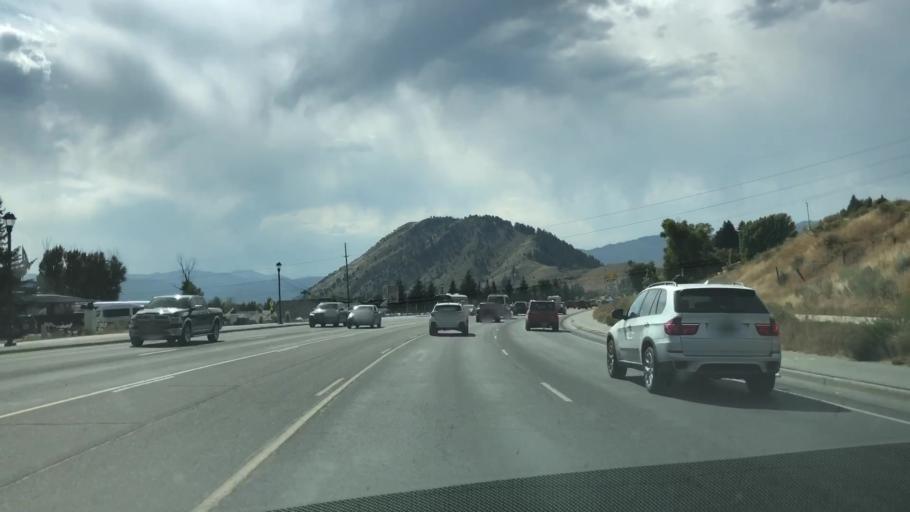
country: US
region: Wyoming
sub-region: Teton County
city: Jackson
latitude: 43.4754
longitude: -110.7751
